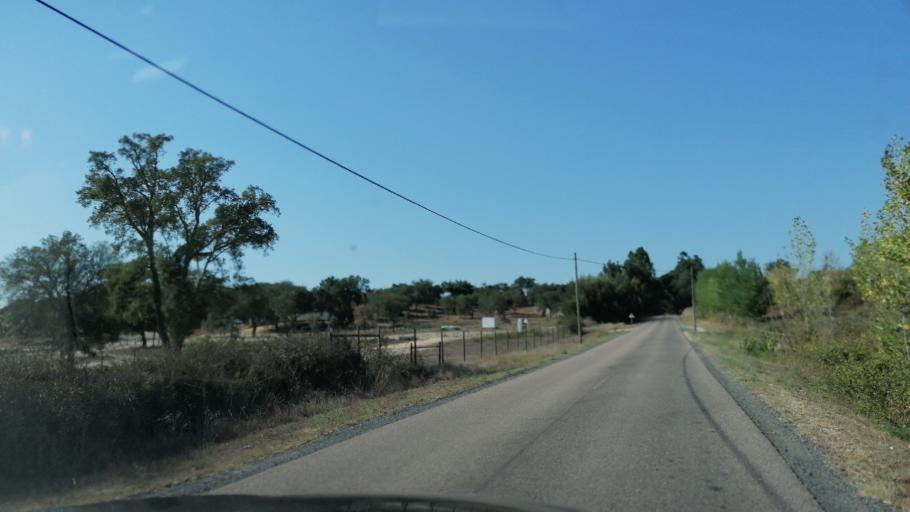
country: PT
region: Santarem
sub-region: Coruche
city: Coruche
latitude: 38.8000
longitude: -8.5788
